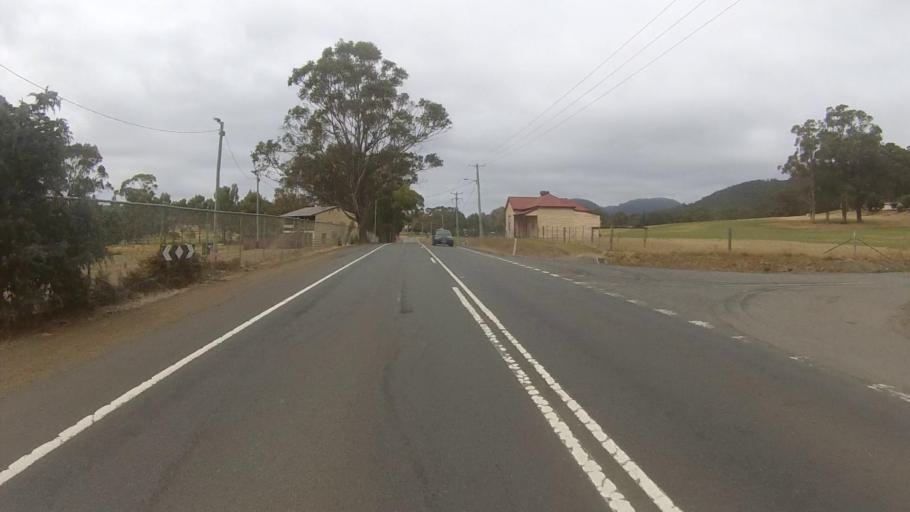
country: AU
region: Tasmania
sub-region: Kingborough
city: Margate
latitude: -42.9884
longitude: 147.1974
